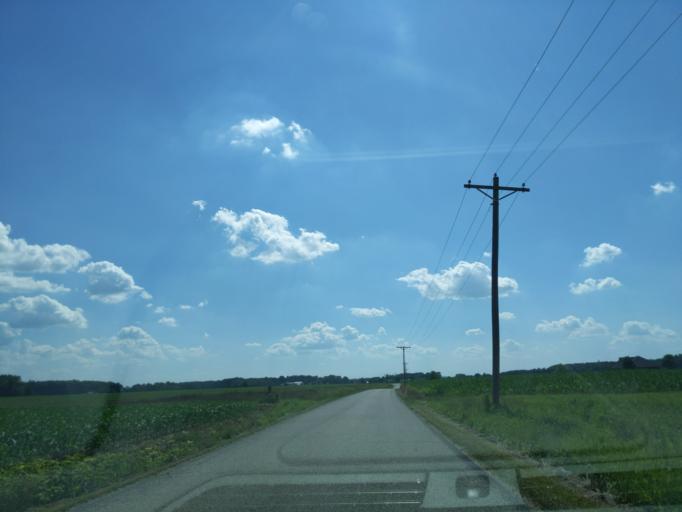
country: US
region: Indiana
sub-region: Ripley County
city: Osgood
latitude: 39.2035
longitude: -85.3608
